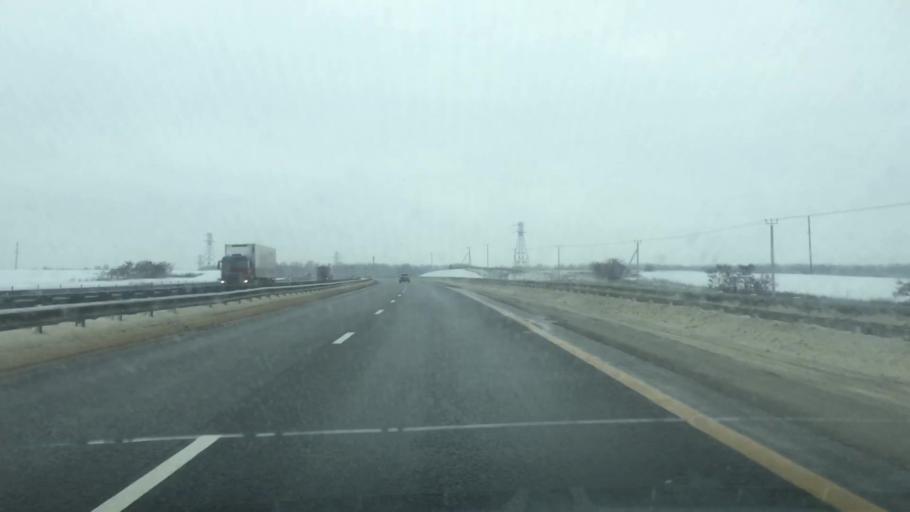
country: RU
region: Tula
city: Yefremov
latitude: 53.1017
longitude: 38.1772
